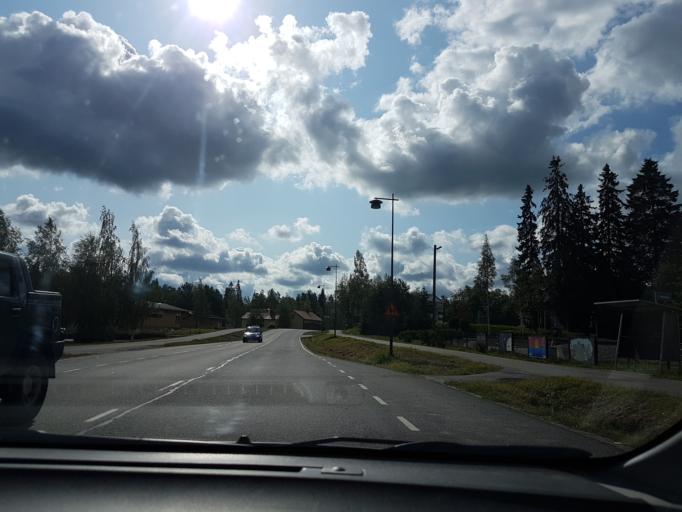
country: FI
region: Uusimaa
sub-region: Helsinki
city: Pornainen
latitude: 60.4805
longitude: 25.3722
